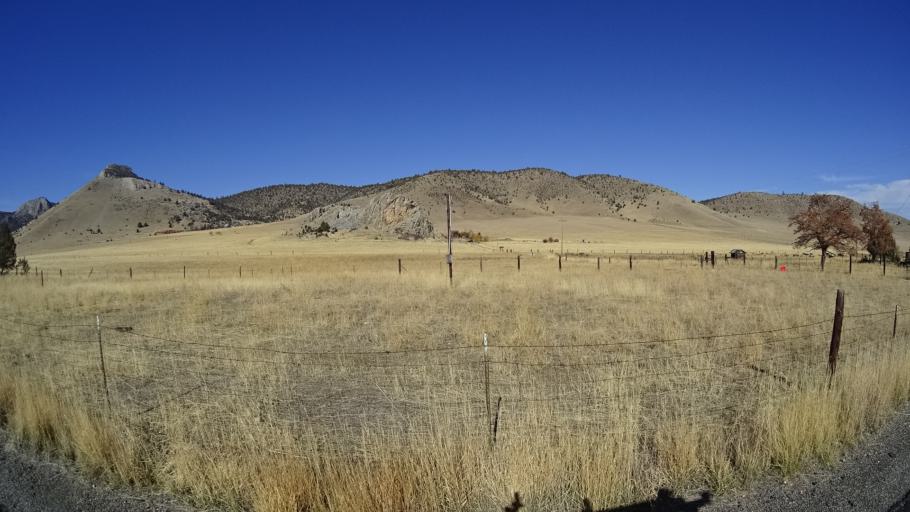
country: US
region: California
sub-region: Siskiyou County
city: Weed
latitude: 41.5032
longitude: -122.5587
